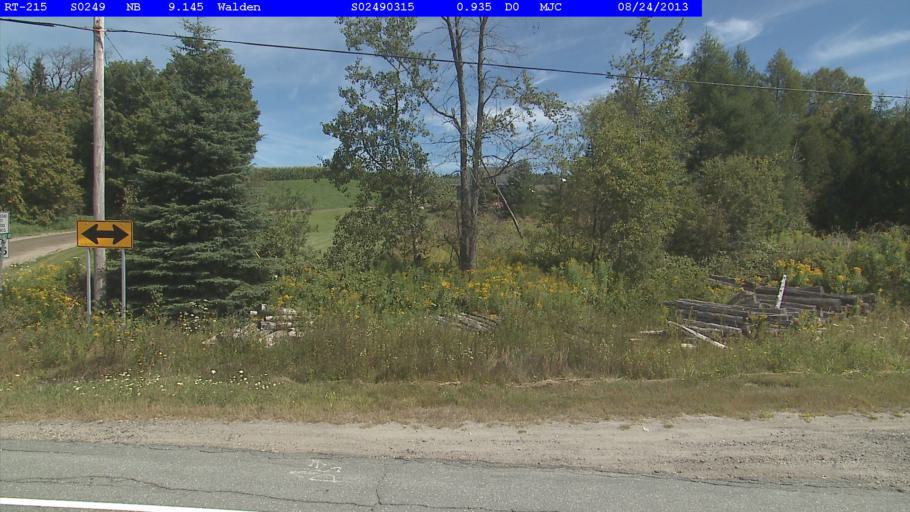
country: US
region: Vermont
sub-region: Caledonia County
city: Hardwick
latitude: 44.4522
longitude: -72.2565
